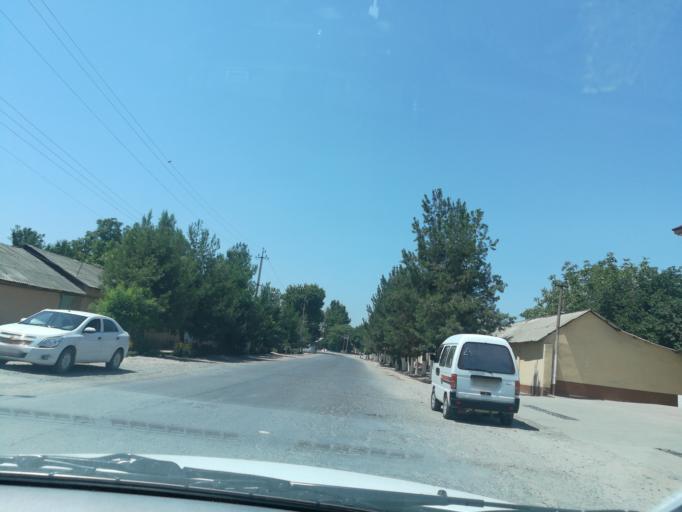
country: UZ
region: Namangan
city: Uchqurghon Shahri
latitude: 41.0615
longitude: 72.0244
